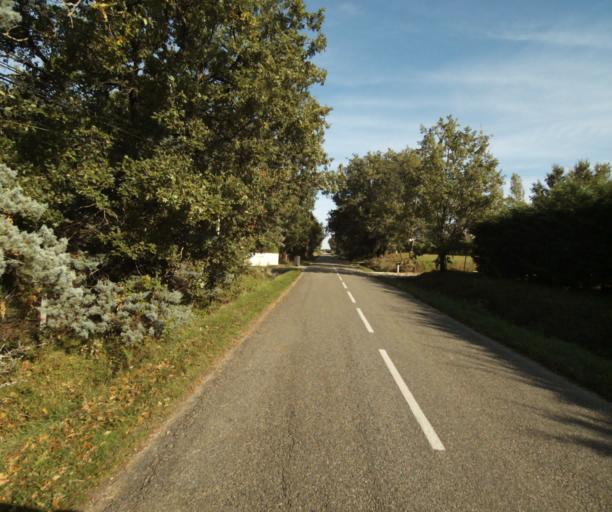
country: FR
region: Midi-Pyrenees
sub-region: Departement du Tarn-et-Garonne
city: Nohic
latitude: 43.9219
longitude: 1.4629
